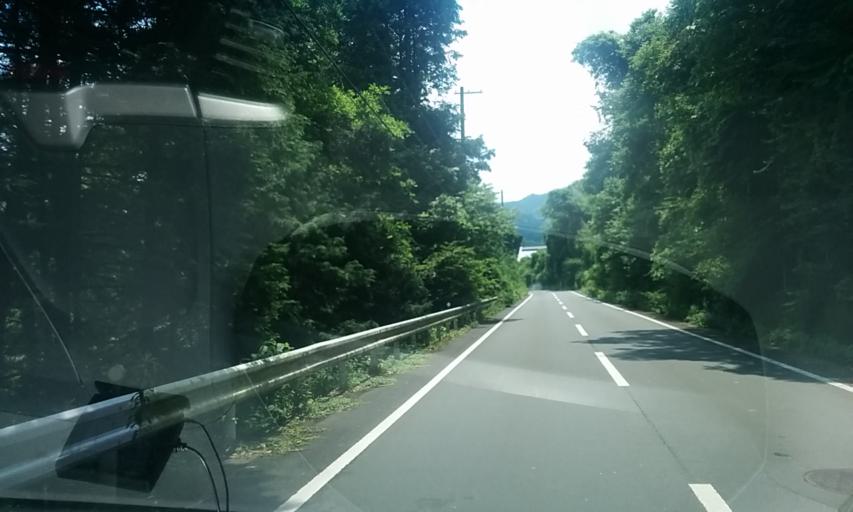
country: JP
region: Kyoto
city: Ayabe
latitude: 35.1844
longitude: 135.2765
